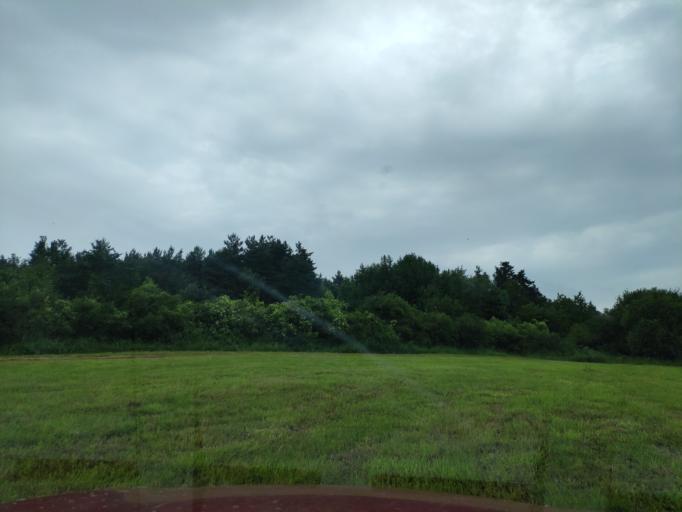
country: SK
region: Presovsky
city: Sabinov
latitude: 49.0528
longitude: 21.0096
